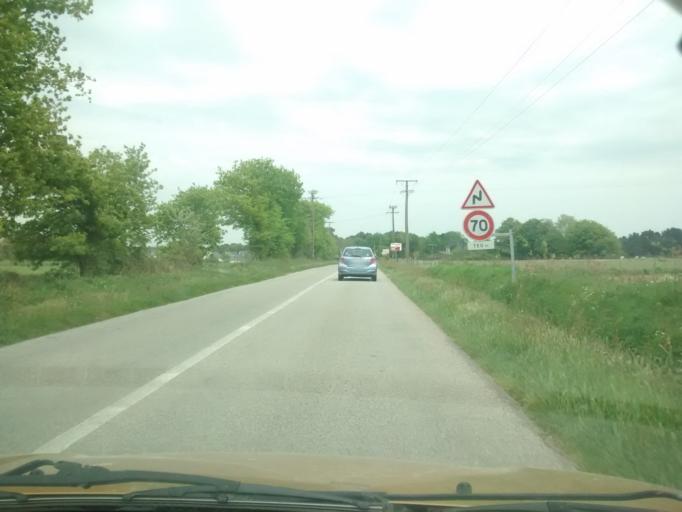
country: FR
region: Brittany
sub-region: Departement du Morbihan
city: Questembert
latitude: 47.6590
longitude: -2.4769
